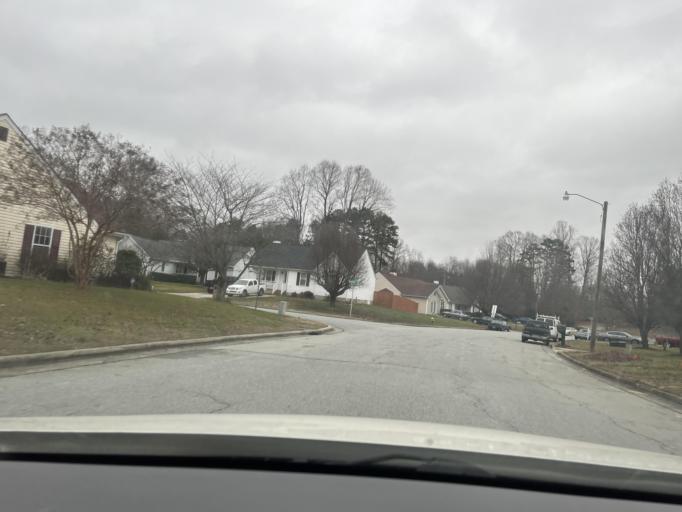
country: US
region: North Carolina
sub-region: Guilford County
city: Pleasant Garden
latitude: 36.0069
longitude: -79.7946
